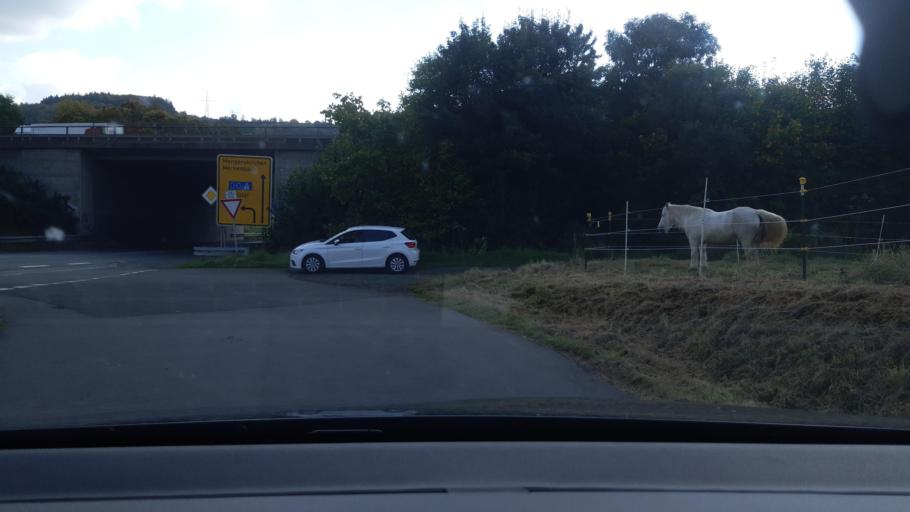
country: DE
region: Hesse
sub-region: Regierungsbezirk Giessen
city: Merkenbach
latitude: 50.6638
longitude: 8.3077
